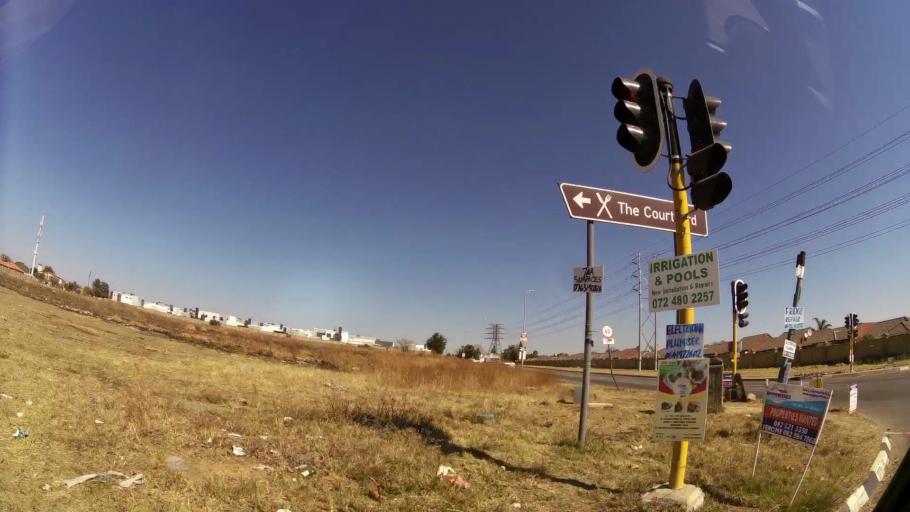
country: ZA
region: Gauteng
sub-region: City of Johannesburg Metropolitan Municipality
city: Midrand
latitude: -25.9640
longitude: 28.1144
